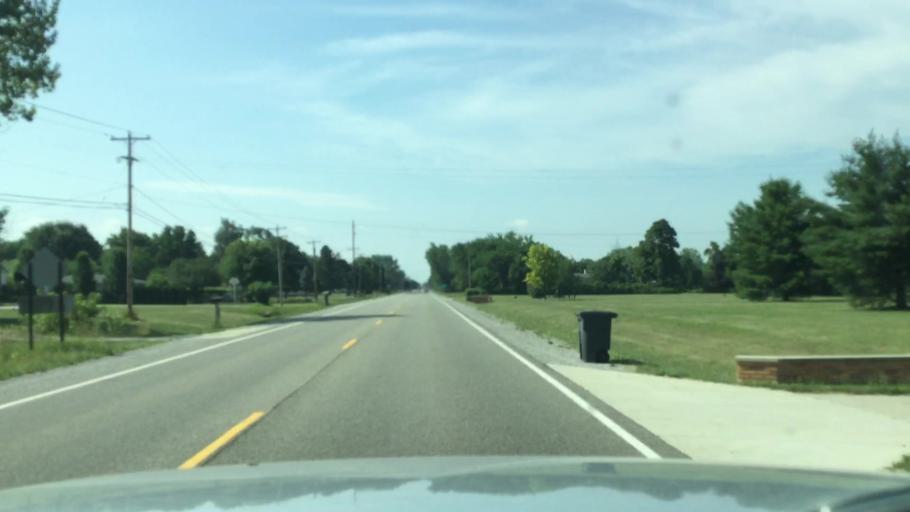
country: US
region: Michigan
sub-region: Genesee County
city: Flushing
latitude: 43.0770
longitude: -83.8134
